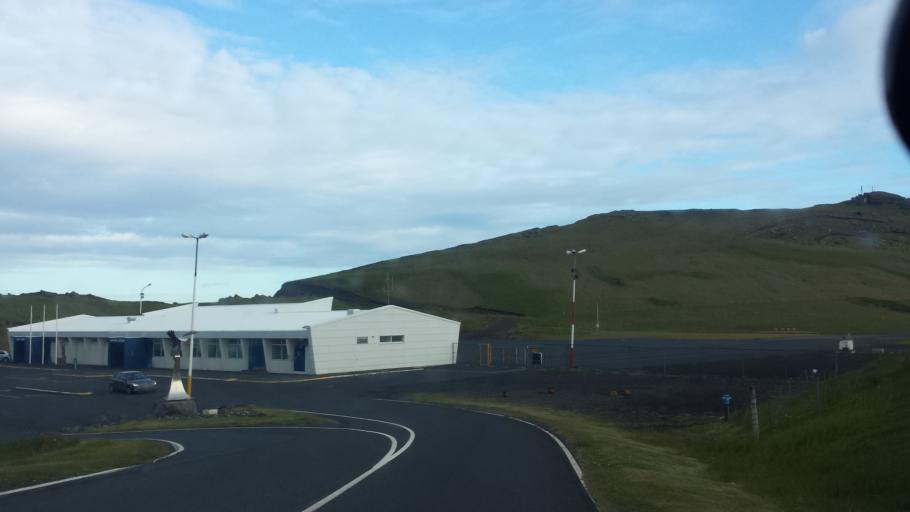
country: IS
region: South
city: Vestmannaeyjar
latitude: 63.4259
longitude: -20.2705
